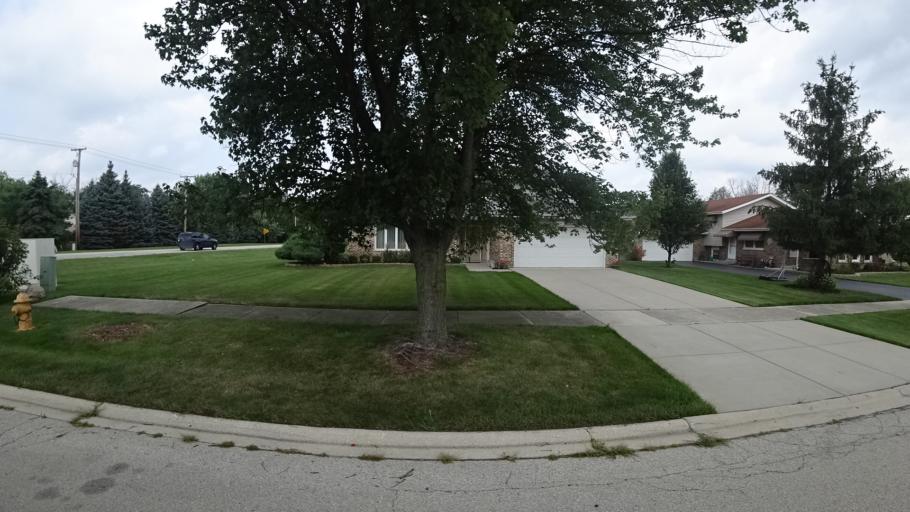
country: US
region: Illinois
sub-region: Will County
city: Goodings Grove
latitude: 41.6336
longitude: -87.9113
